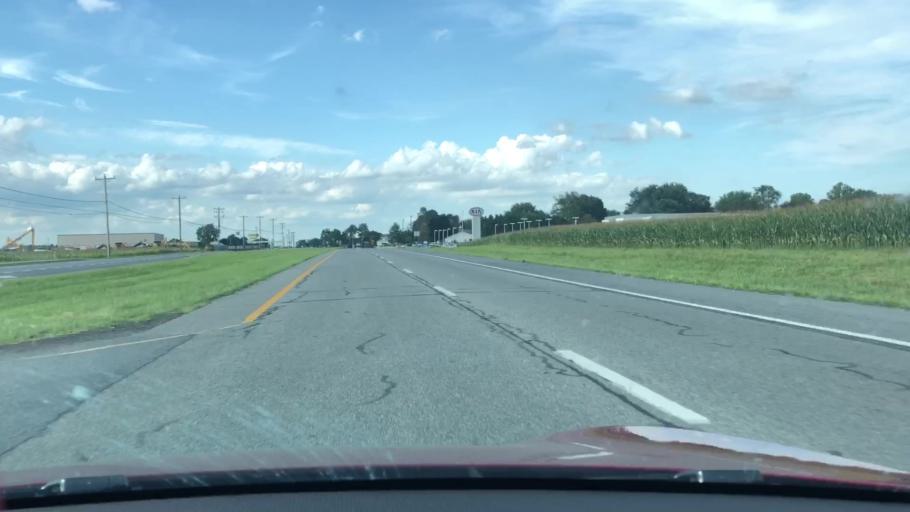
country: US
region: Delaware
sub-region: Kent County
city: Felton
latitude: 38.9791
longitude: -75.5670
